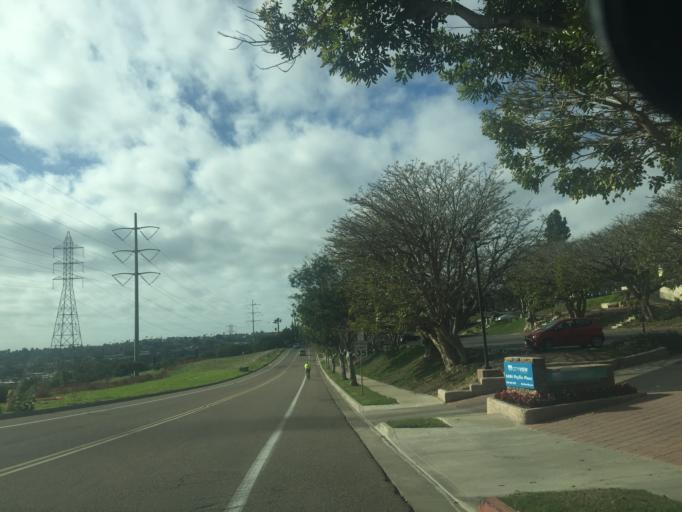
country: US
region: California
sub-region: San Diego County
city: San Diego
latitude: 32.7843
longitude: -117.1468
